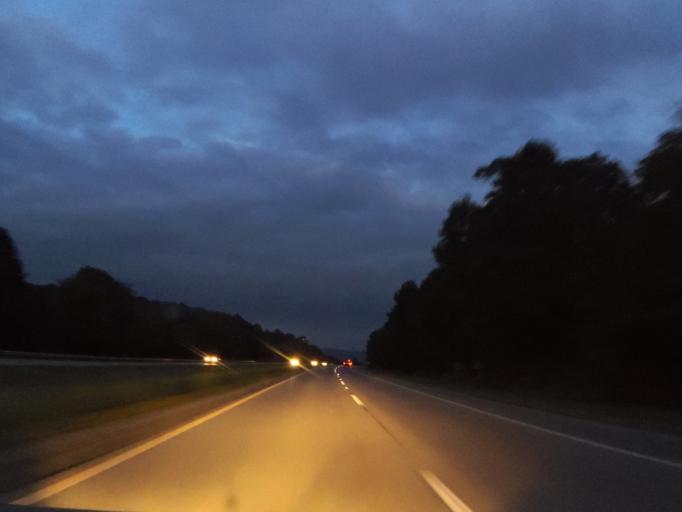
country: US
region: Alabama
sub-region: Jackson County
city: Scottsboro
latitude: 34.6235
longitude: -86.1955
